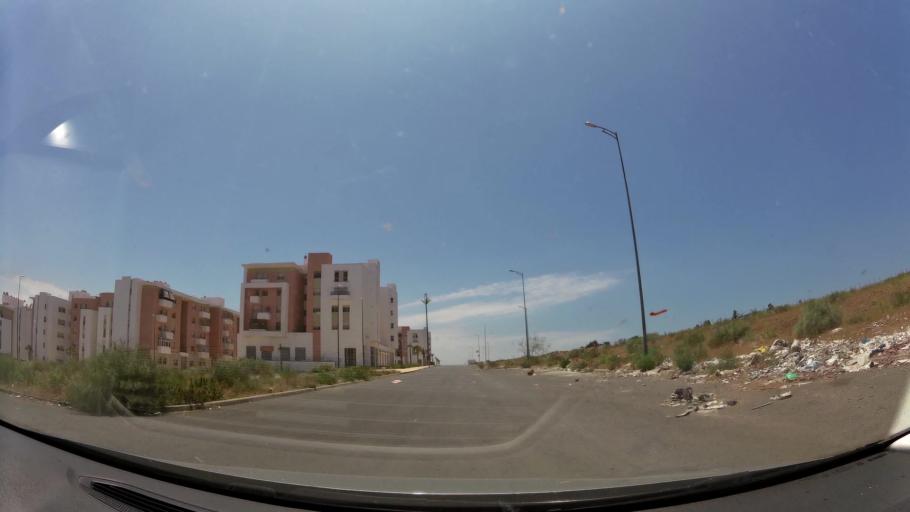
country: MA
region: Gharb-Chrarda-Beni Hssen
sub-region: Kenitra Province
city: Kenitra
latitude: 34.2549
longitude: -6.6572
